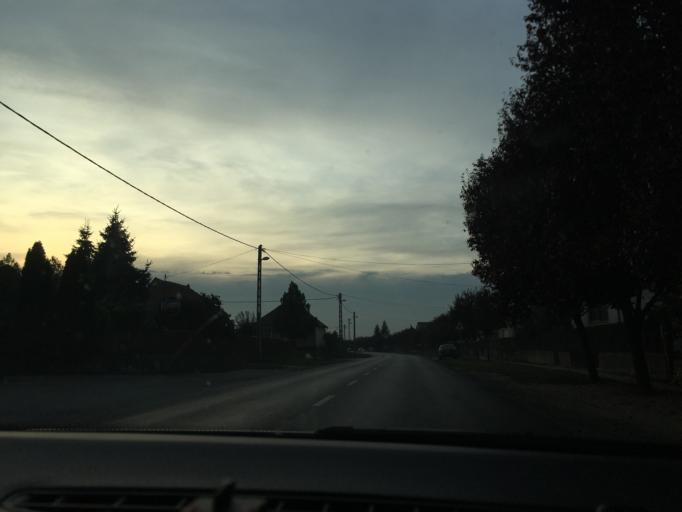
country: HU
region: Szabolcs-Szatmar-Bereg
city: Kallosemjen
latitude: 47.8595
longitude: 21.9162
